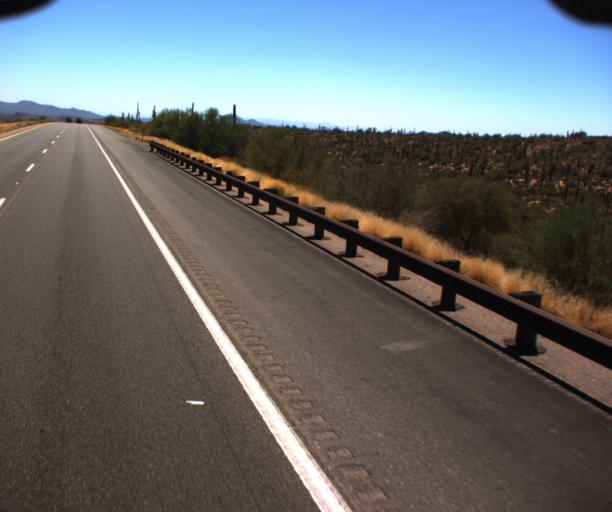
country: US
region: Arizona
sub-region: Maricopa County
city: Rio Verde
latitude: 33.6594
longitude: -111.5205
